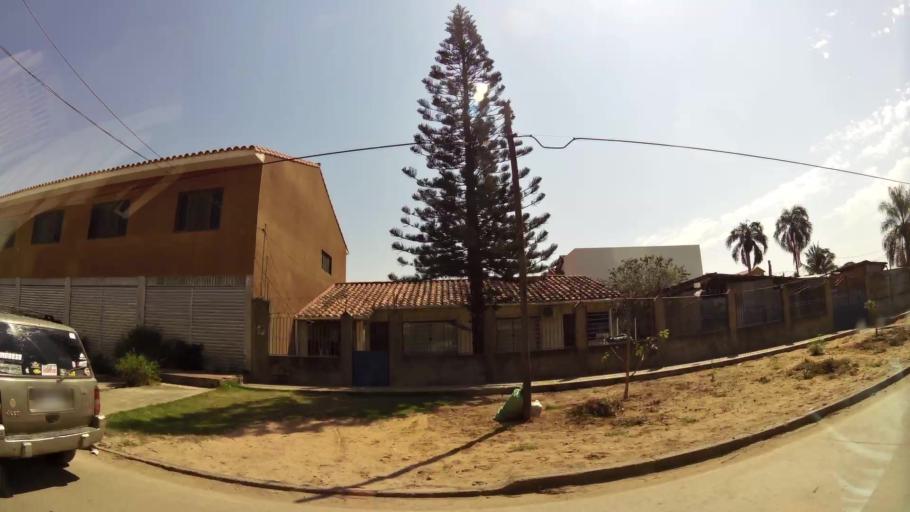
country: BO
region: Santa Cruz
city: Santa Cruz de la Sierra
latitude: -17.7436
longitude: -63.1551
